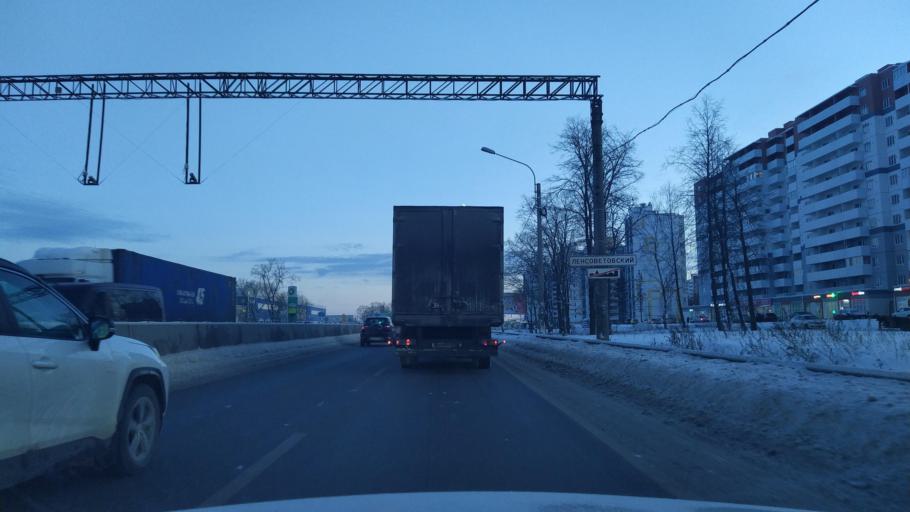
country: RU
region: St.-Petersburg
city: Petro-Slavyanka
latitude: 59.7627
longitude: 30.4707
